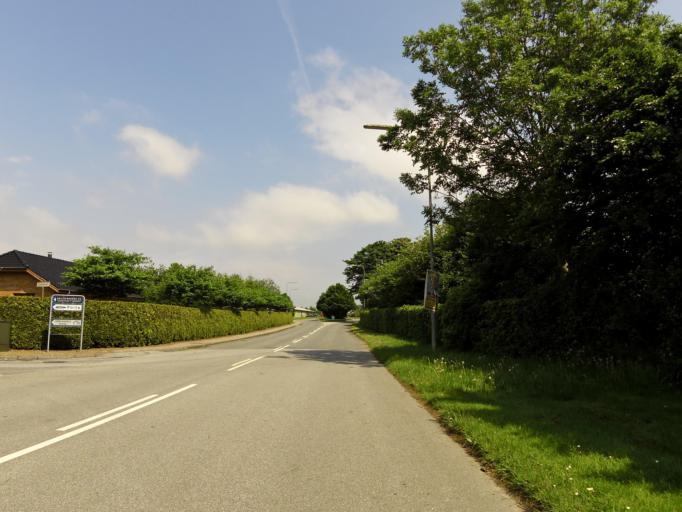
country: DK
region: South Denmark
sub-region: Tonder Kommune
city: Toftlund
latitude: 55.1897
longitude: 9.0758
